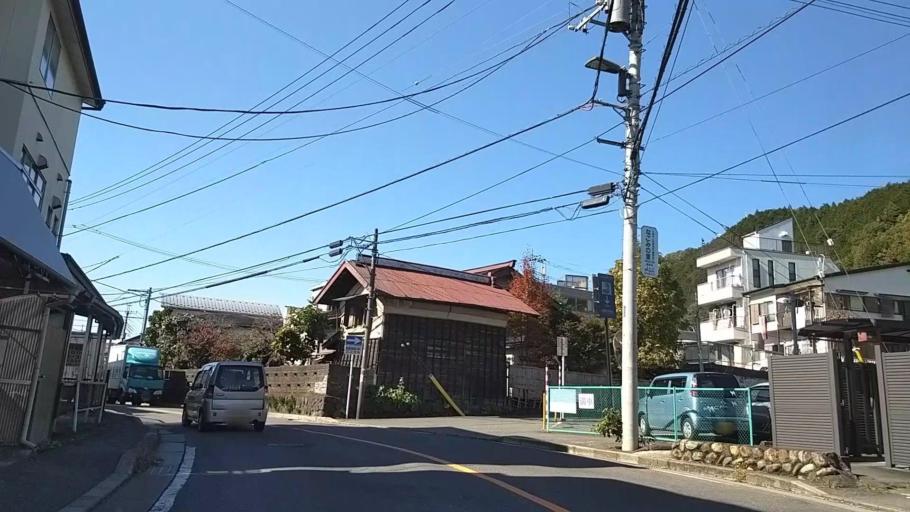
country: JP
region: Yamanashi
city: Uenohara
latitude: 35.6153
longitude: 139.1531
